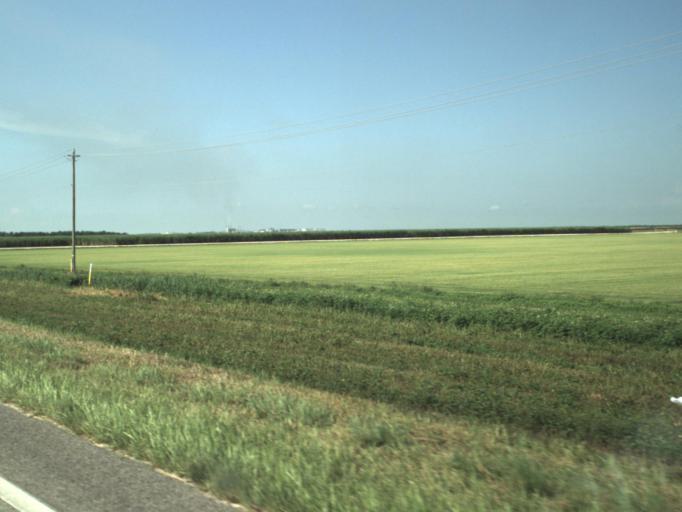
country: US
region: Florida
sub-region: Palm Beach County
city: South Bay
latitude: 26.6340
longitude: -80.7124
